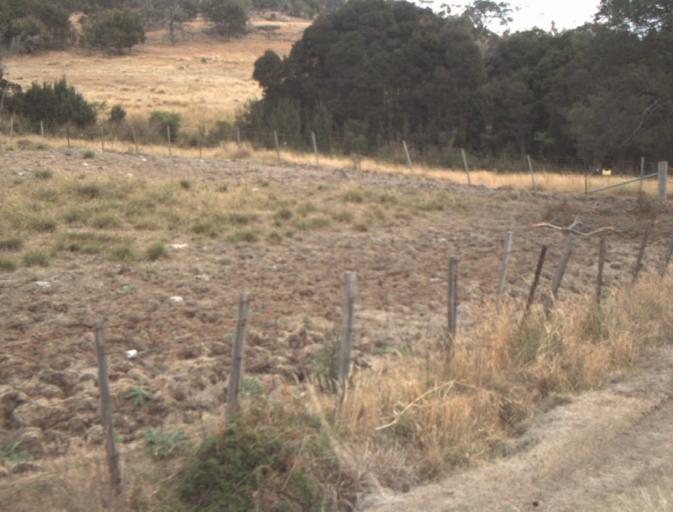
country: AU
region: Tasmania
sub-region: Launceston
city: Mayfield
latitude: -41.2830
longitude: 147.0268
